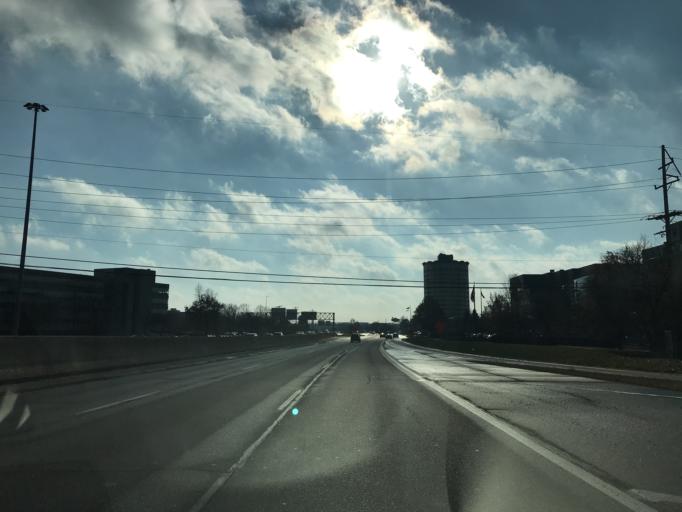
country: US
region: Michigan
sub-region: Oakland County
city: Bingham Farms
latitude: 42.4871
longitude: -83.2848
